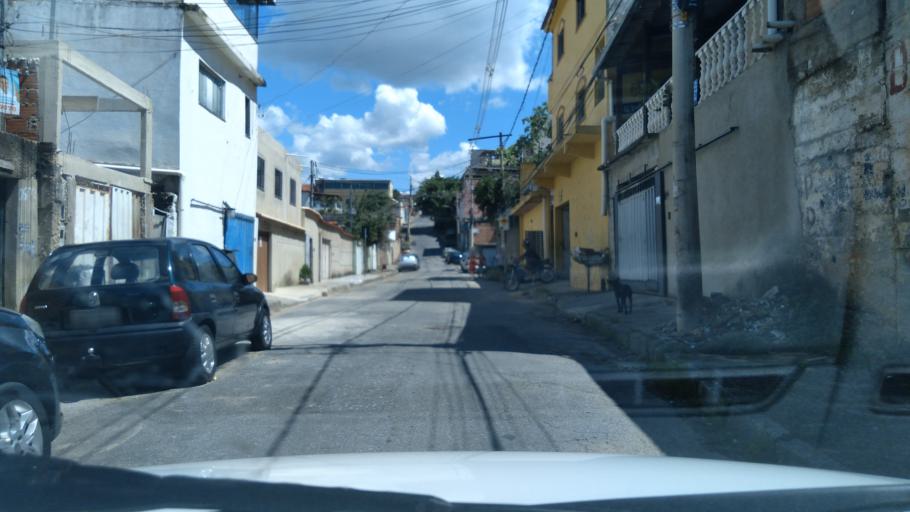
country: BR
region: Minas Gerais
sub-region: Belo Horizonte
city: Belo Horizonte
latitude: -19.8680
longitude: -43.9157
